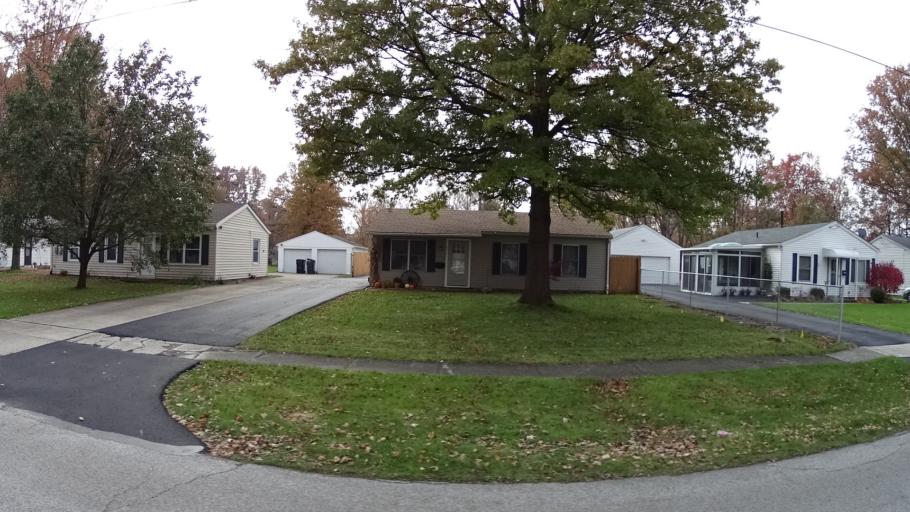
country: US
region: Ohio
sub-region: Lorain County
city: Elyria
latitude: 41.3596
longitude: -82.0855
